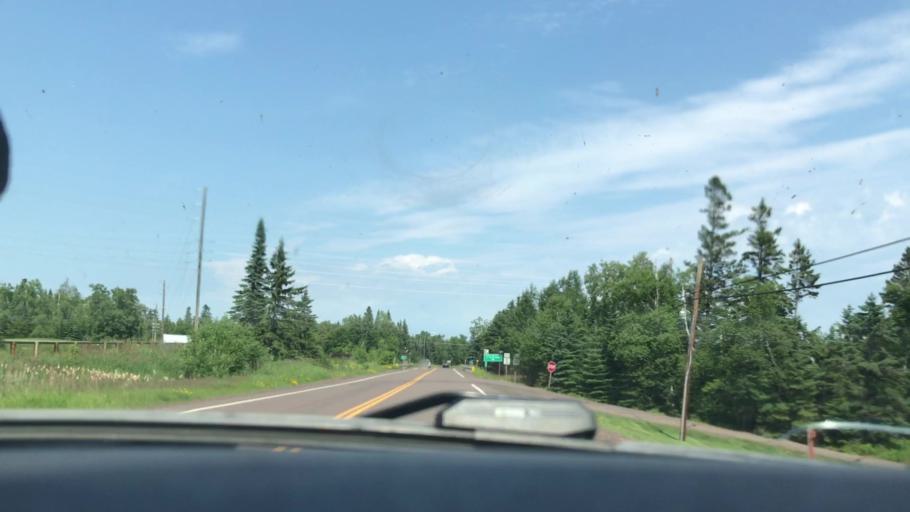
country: US
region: Minnesota
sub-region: Cook County
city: Grand Marais
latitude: 47.6380
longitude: -90.7099
